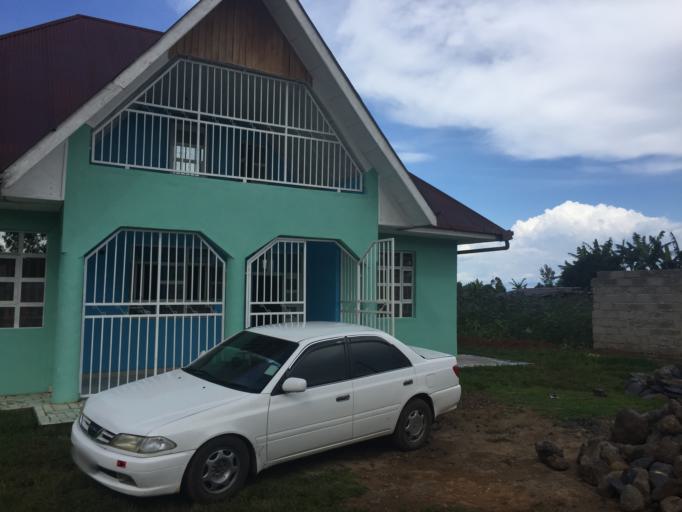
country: CD
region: South Kivu
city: Bukavu
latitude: -2.4011
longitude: 28.8062
